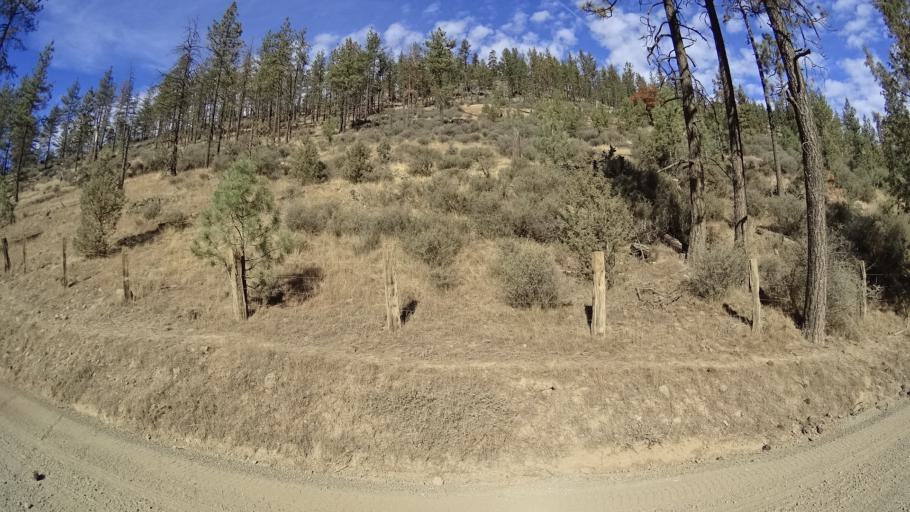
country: US
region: California
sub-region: Siskiyou County
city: Yreka
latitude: 41.6146
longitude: -122.7232
